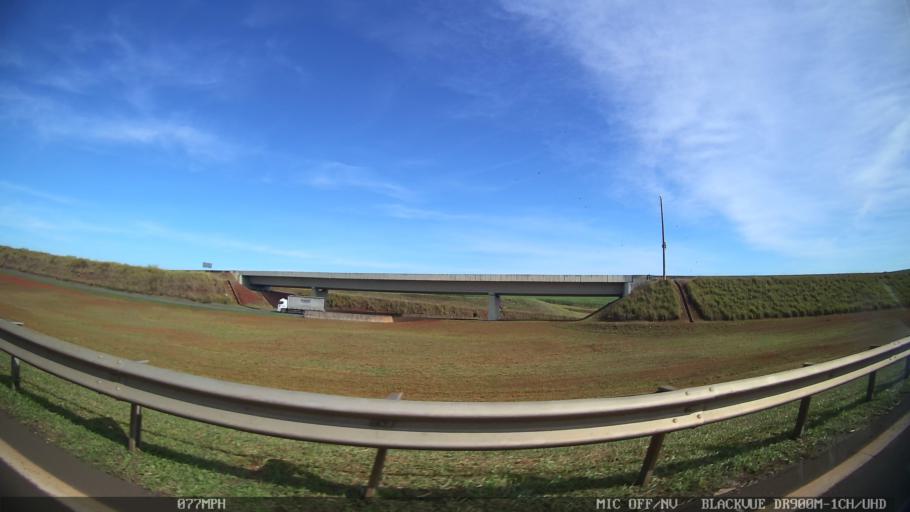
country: BR
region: Sao Paulo
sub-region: Cordeiropolis
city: Cordeiropolis
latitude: -22.4820
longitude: -47.3991
